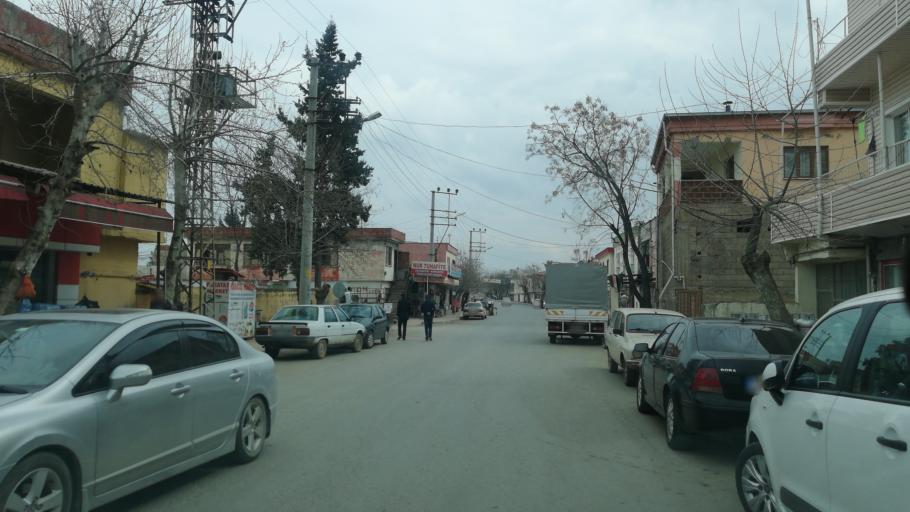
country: TR
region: Kahramanmaras
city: Turkoglu
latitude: 37.4122
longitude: 36.8797
